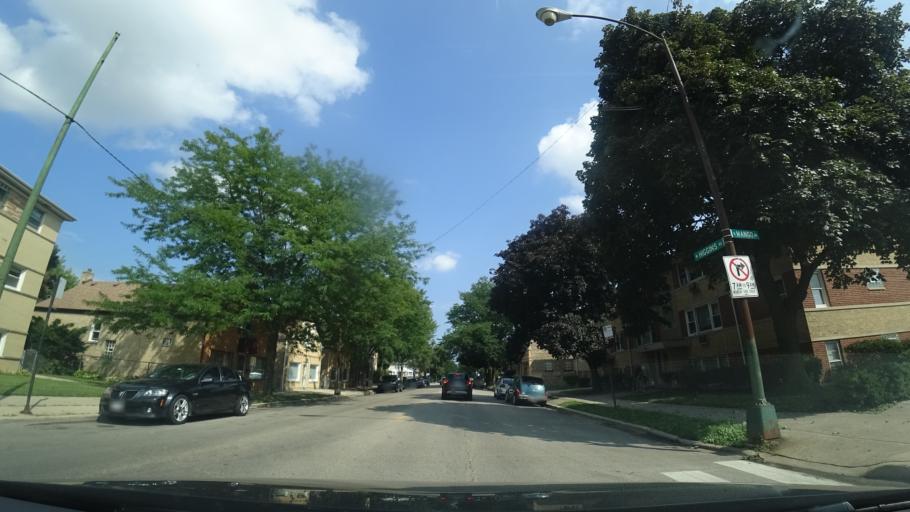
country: US
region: Illinois
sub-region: Cook County
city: Harwood Heights
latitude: 41.9712
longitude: -87.7724
